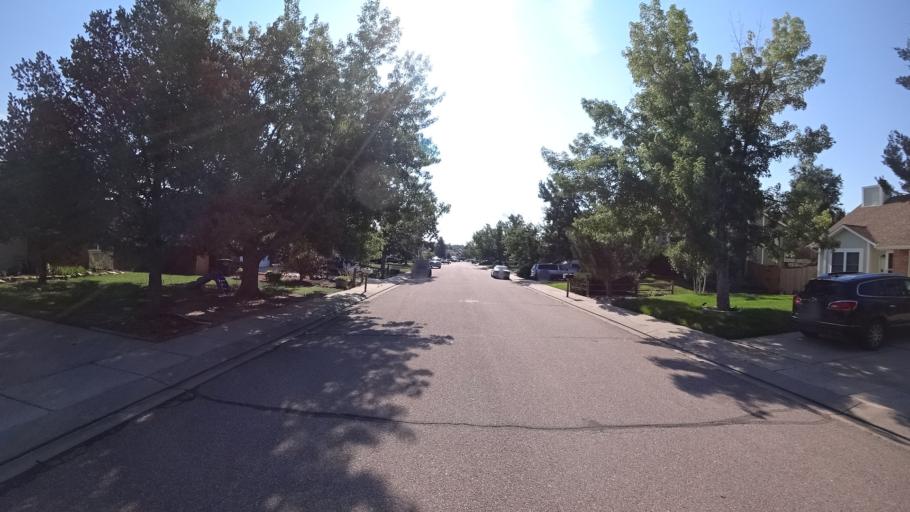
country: US
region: Colorado
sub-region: El Paso County
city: Black Forest
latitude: 38.9461
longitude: -104.7696
